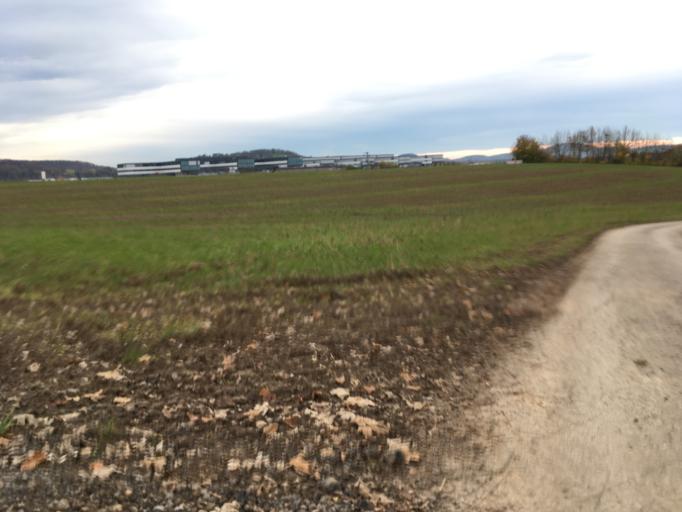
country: DE
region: Baden-Wuerttemberg
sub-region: Regierungsbezirk Stuttgart
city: Abstatt
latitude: 49.0843
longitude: 9.3026
